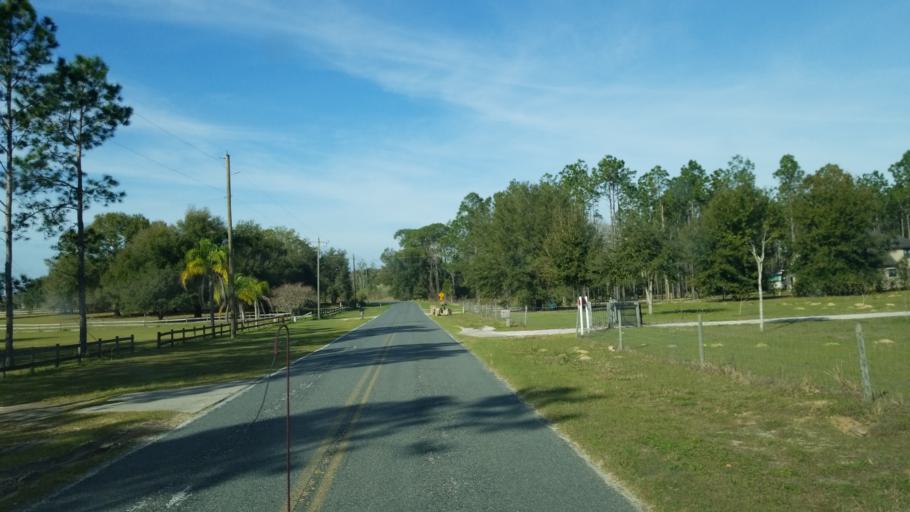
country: US
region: Florida
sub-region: Lake County
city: Clermont
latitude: 28.4451
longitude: -81.7888
